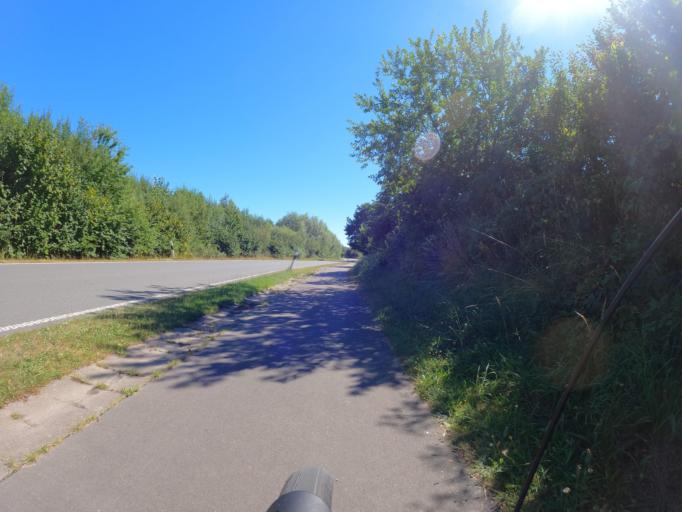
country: DE
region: Schleswig-Holstein
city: Quern
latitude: 54.7897
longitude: 9.7243
